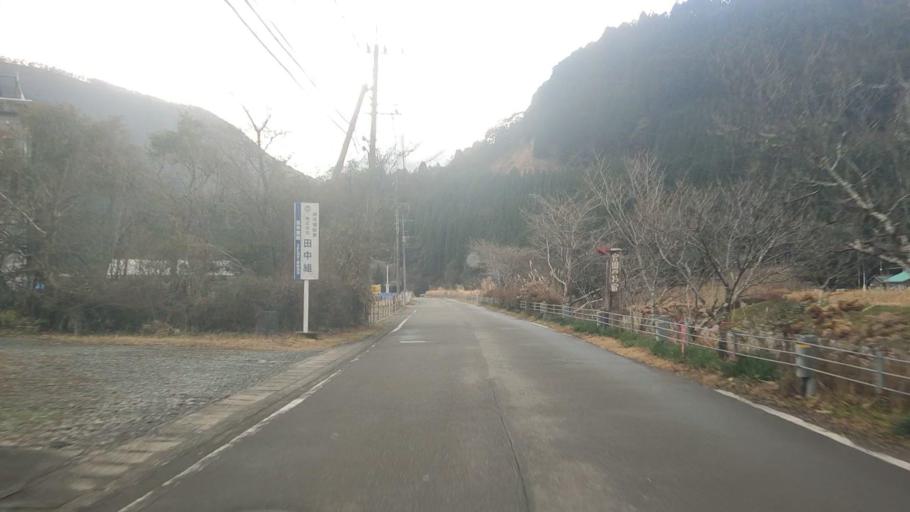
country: JP
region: Kumamoto
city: Hitoyoshi
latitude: 32.4389
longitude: 130.8569
